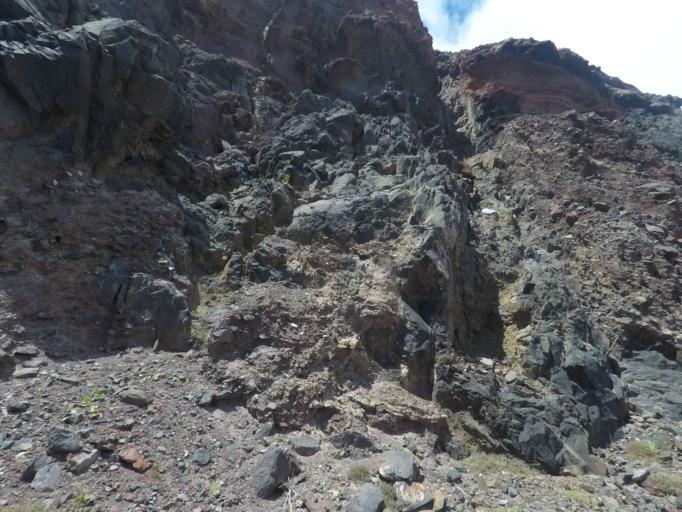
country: PT
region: Madeira
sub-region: Porto Santo
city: Vila de Porto Santo
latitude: 33.0605
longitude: -16.2978
